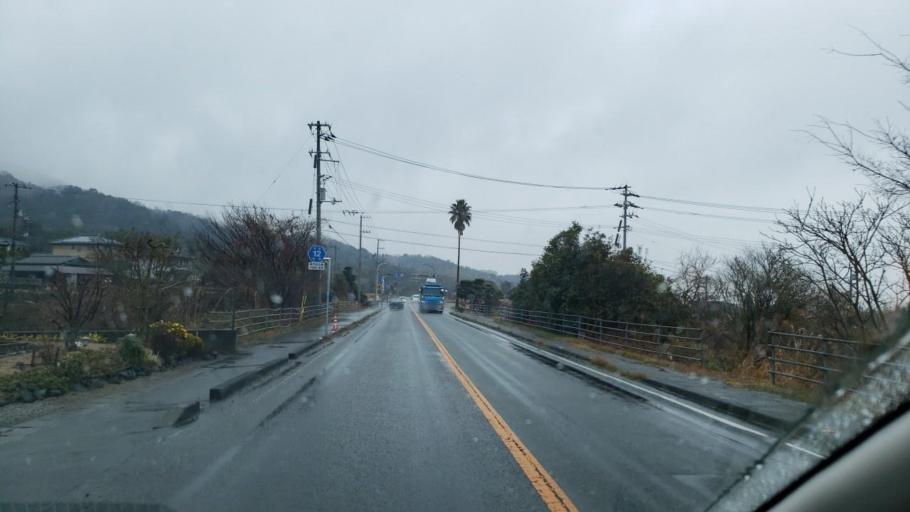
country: JP
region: Tokushima
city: Tokushima-shi
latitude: 34.1561
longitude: 134.5113
